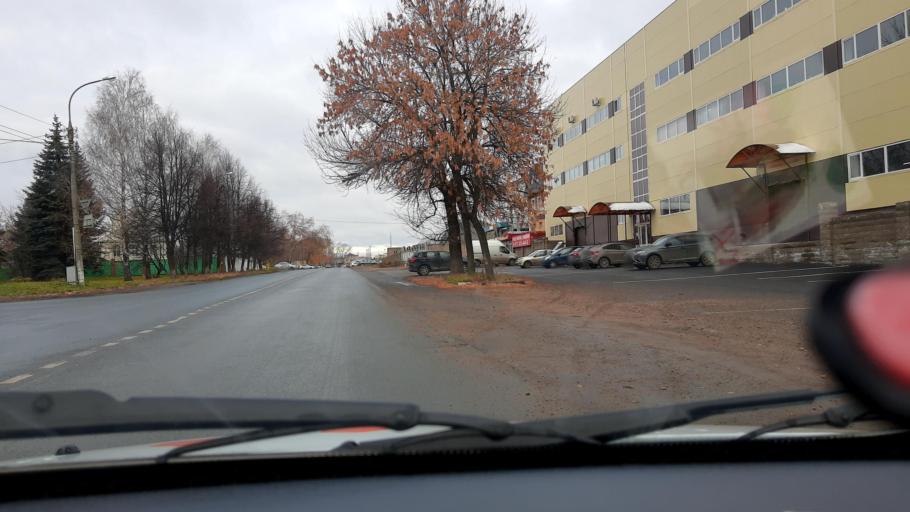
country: RU
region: Bashkortostan
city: Ufa
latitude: 54.8001
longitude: 56.1093
